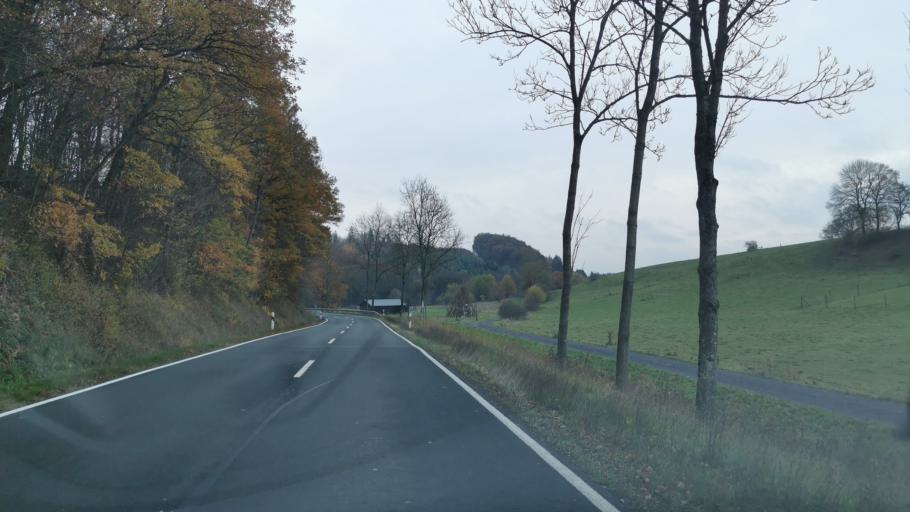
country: DE
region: Rheinland-Pfalz
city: Schonbach
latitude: 50.2138
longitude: 6.9509
